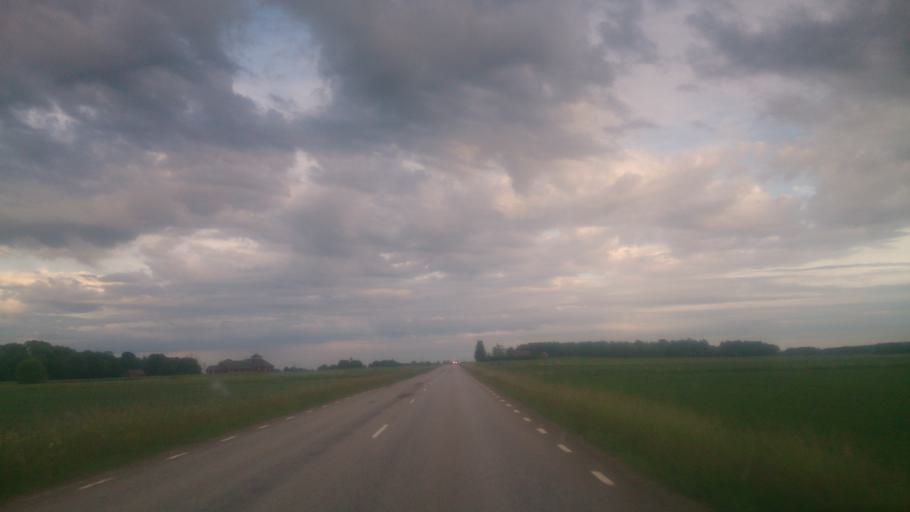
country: SE
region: OEstergoetland
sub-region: Motala Kommun
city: Borensberg
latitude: 58.5046
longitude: 15.2003
